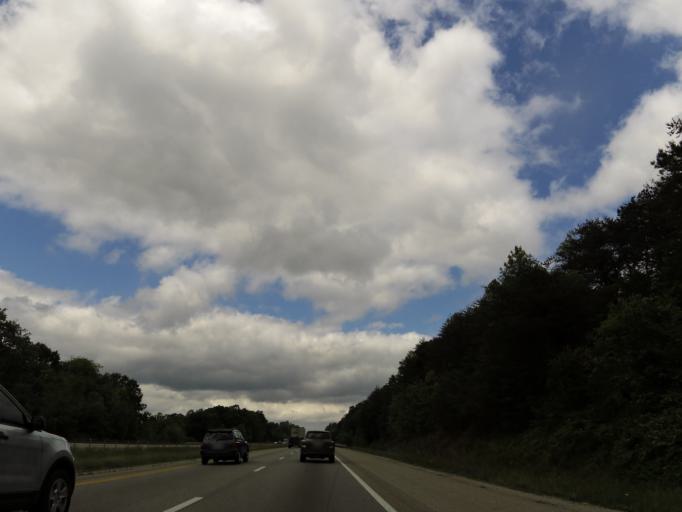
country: US
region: Kentucky
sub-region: Laurel County
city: North Corbin
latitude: 37.0081
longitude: -84.1033
